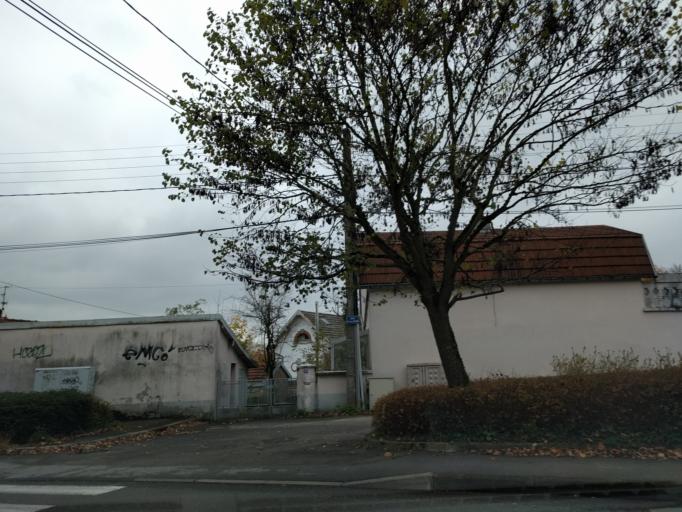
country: FR
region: Franche-Comte
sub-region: Departement du Doubs
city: Besancon
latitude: 47.2553
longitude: 6.0229
